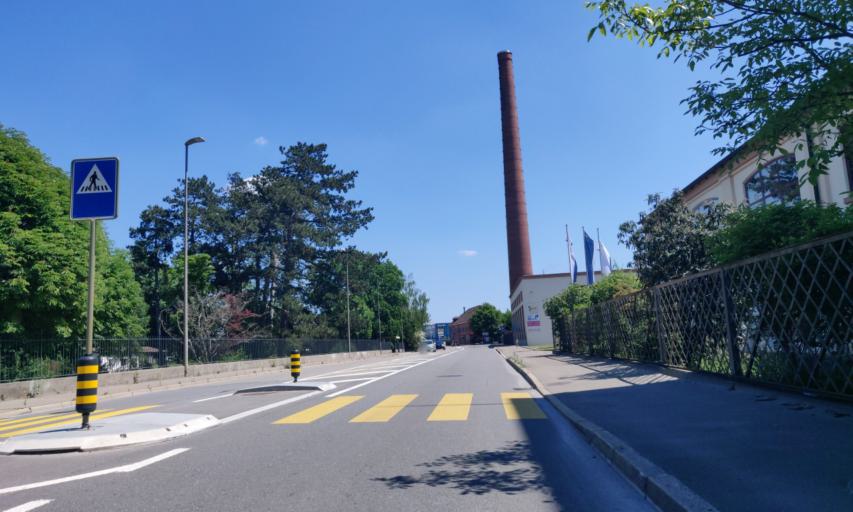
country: DE
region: Baden-Wuerttemberg
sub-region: Freiburg Region
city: Grenzach-Wyhlen
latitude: 47.5316
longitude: 7.6755
